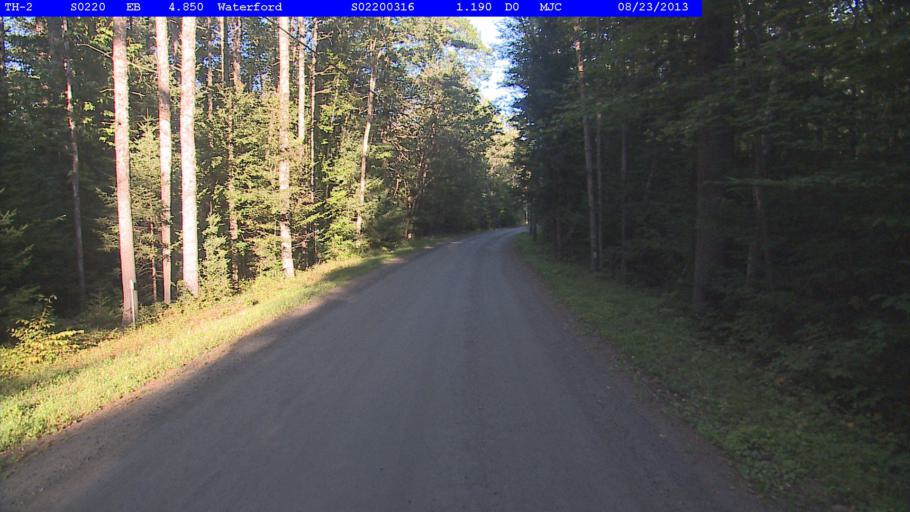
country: US
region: Vermont
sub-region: Caledonia County
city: Saint Johnsbury
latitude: 44.3435
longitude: -71.9754
